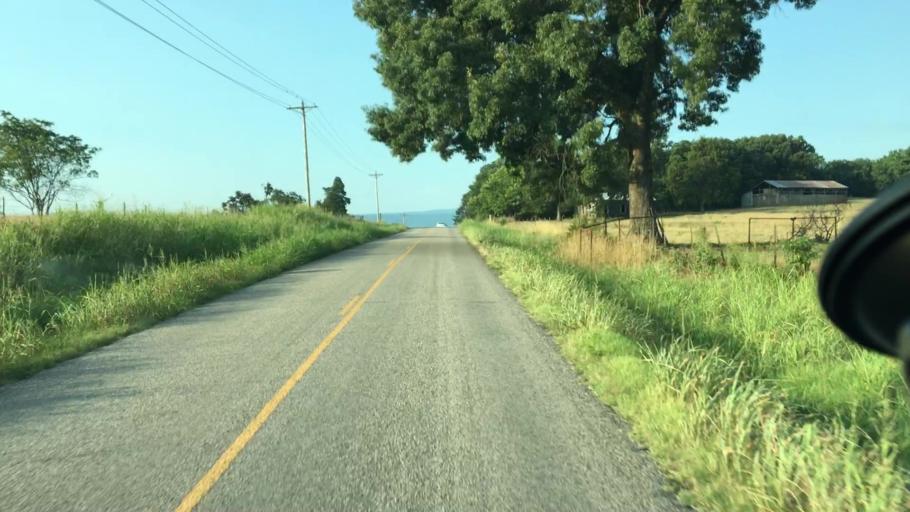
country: US
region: Arkansas
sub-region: Johnson County
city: Coal Hill
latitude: 35.3520
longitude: -93.6133
